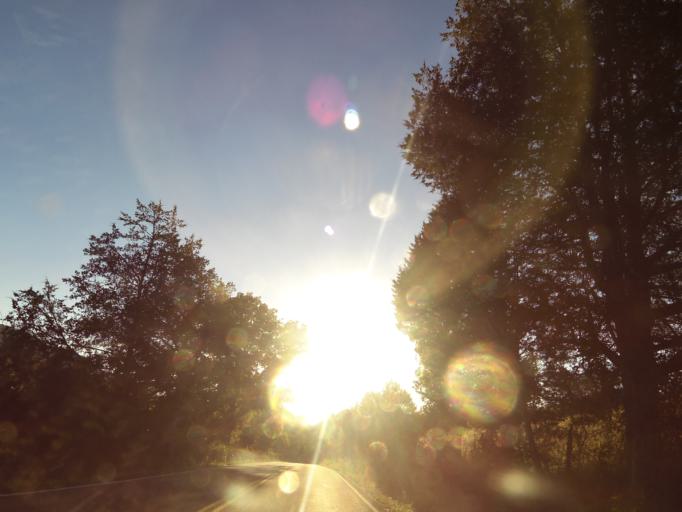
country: US
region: Tennessee
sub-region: Grainger County
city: Rutledge
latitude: 36.3474
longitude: -83.4560
